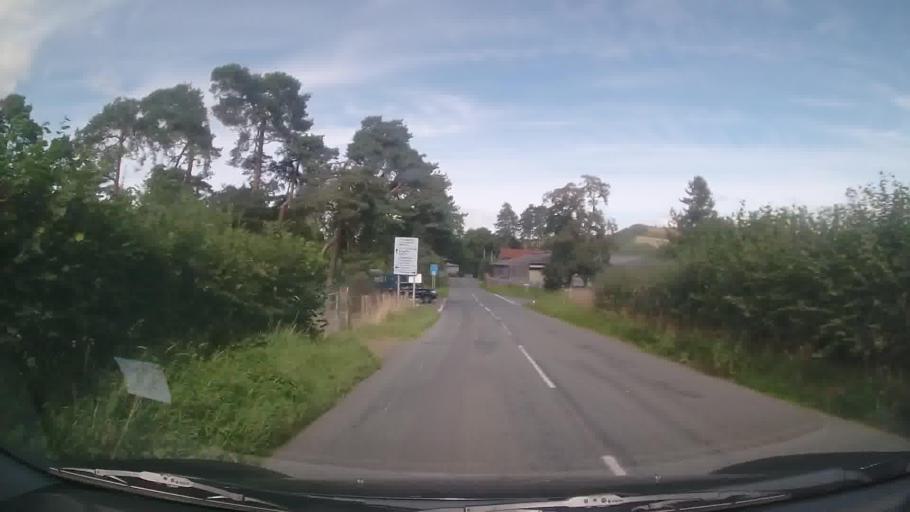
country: GB
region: Wales
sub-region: Sir Powys
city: Whitton
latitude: 52.2797
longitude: -3.0753
